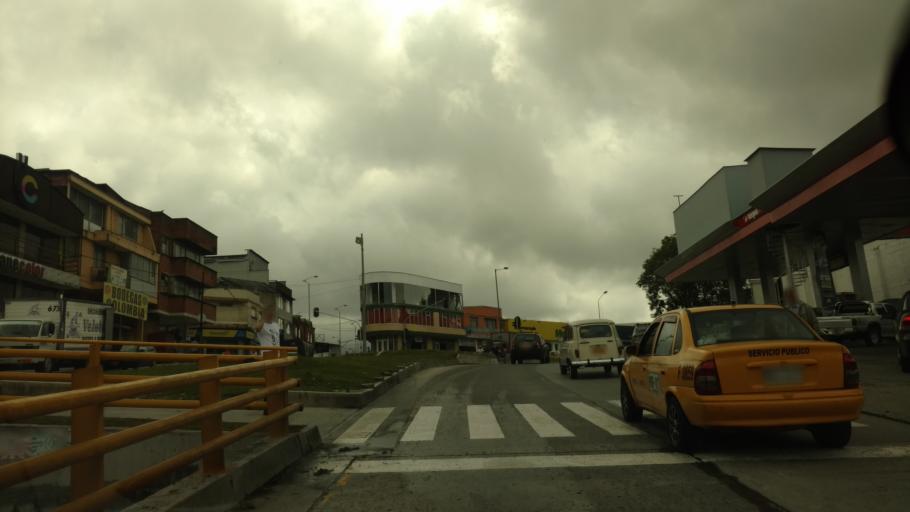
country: CO
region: Caldas
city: Manizales
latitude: 5.0704
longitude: -75.5145
